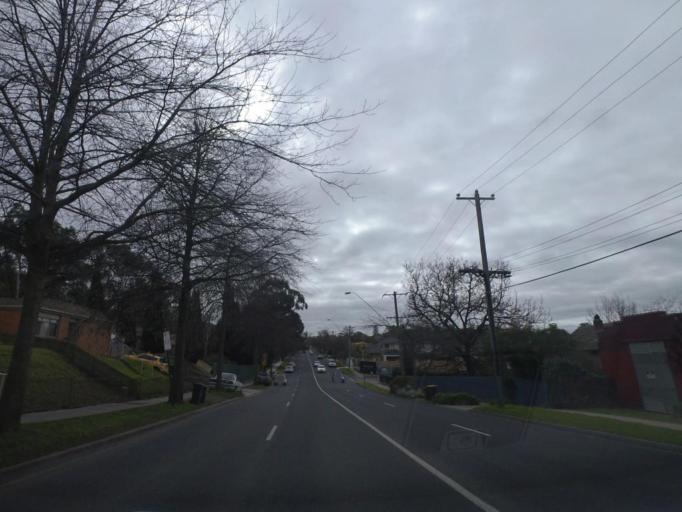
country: AU
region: Victoria
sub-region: Whitehorse
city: Burwood
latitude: -37.8433
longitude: 145.1101
